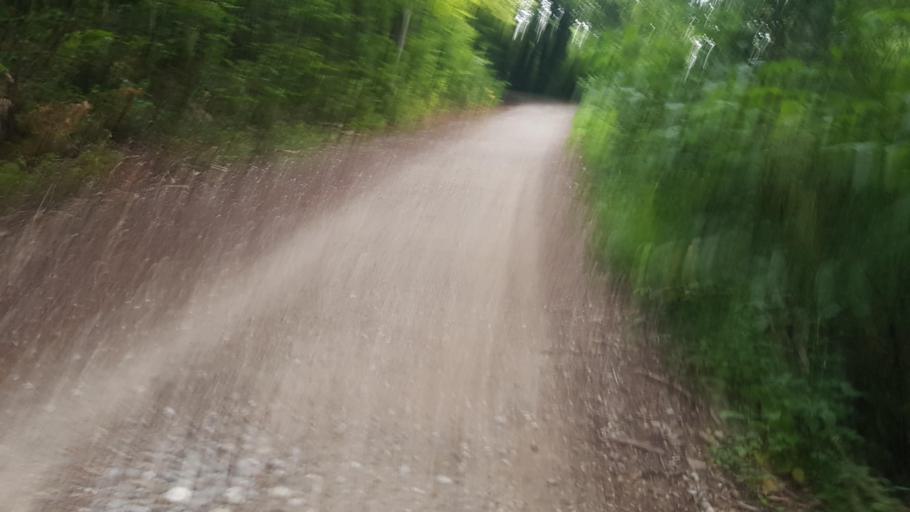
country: DE
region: Bavaria
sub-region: Upper Bavaria
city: Starnberg
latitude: 48.0321
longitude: 11.3536
